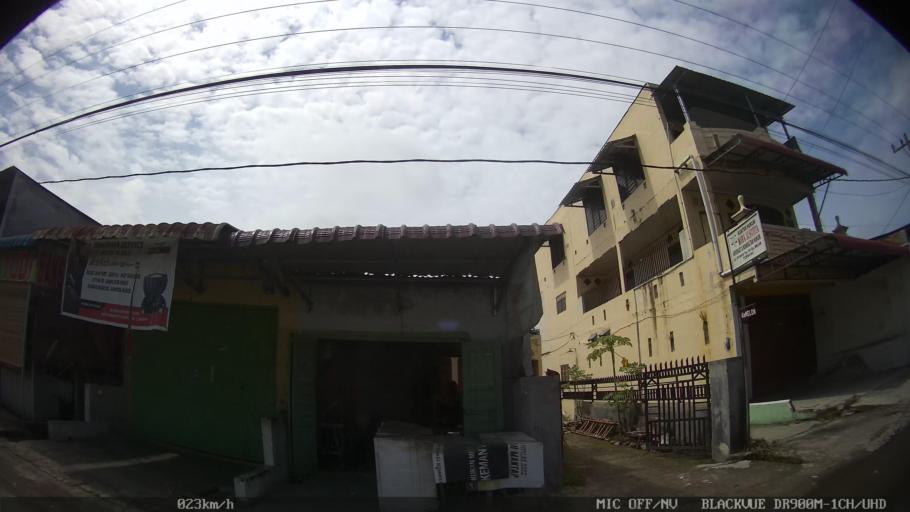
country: ID
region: North Sumatra
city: Medan
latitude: 3.5895
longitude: 98.7488
